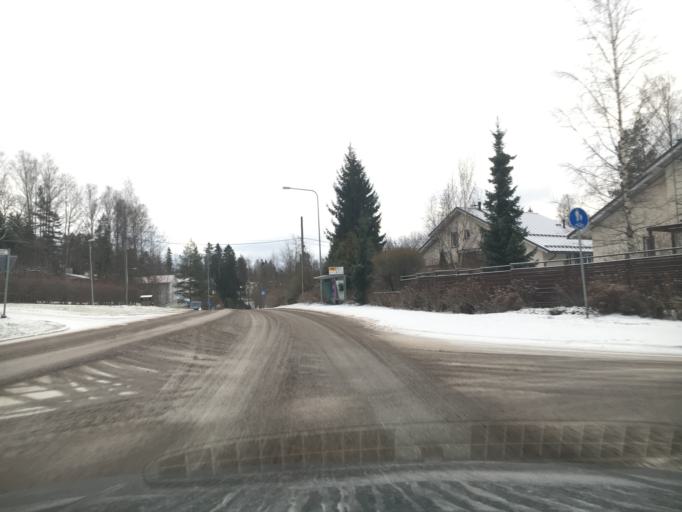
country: FI
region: Uusimaa
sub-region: Helsinki
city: Espoo
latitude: 60.1652
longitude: 24.6513
